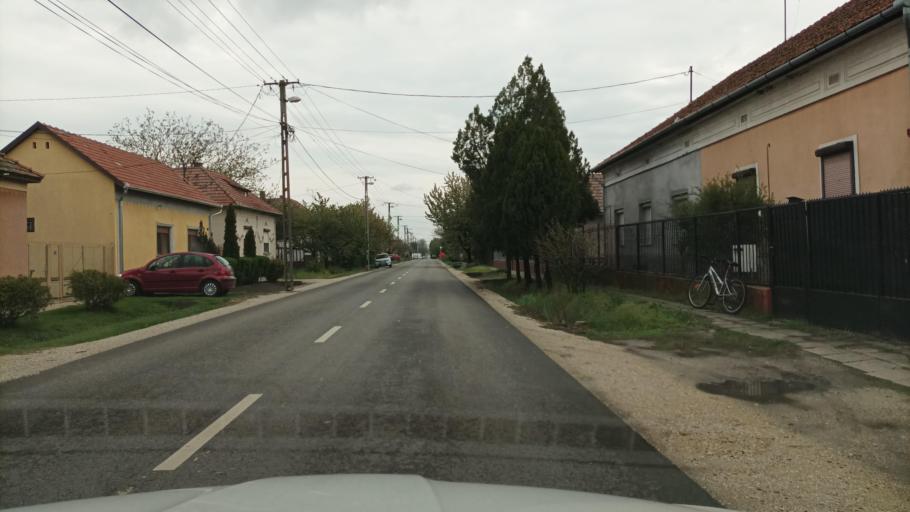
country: HU
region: Pest
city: Kocser
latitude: 47.0039
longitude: 19.9155
